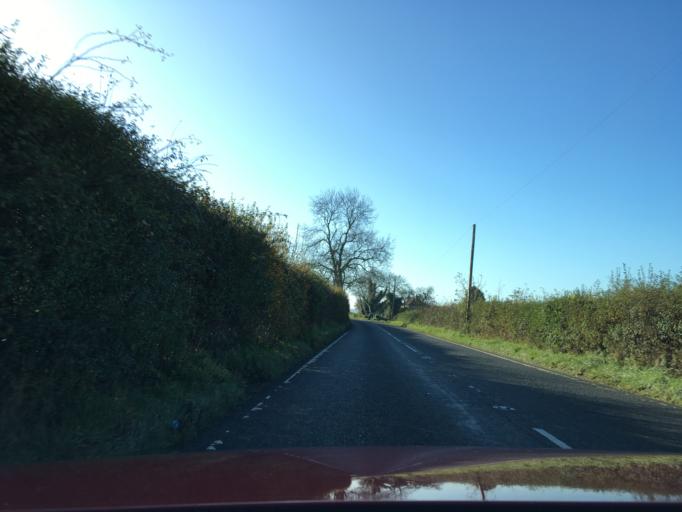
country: GB
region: England
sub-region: Somerset
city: Langport
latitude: 51.0728
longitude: -2.8545
